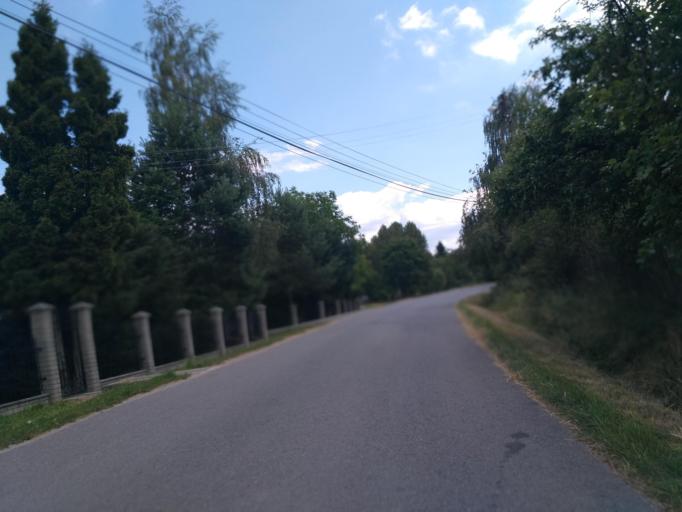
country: PL
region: Subcarpathian Voivodeship
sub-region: Powiat debicki
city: Brzostek
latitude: 49.8616
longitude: 21.4597
